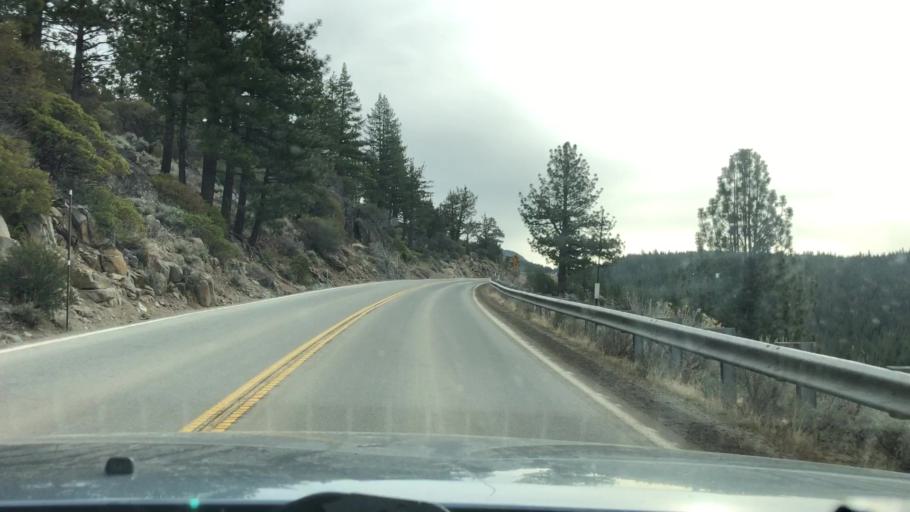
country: US
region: California
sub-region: Nevada County
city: Truckee
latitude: 39.5571
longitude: -120.3435
